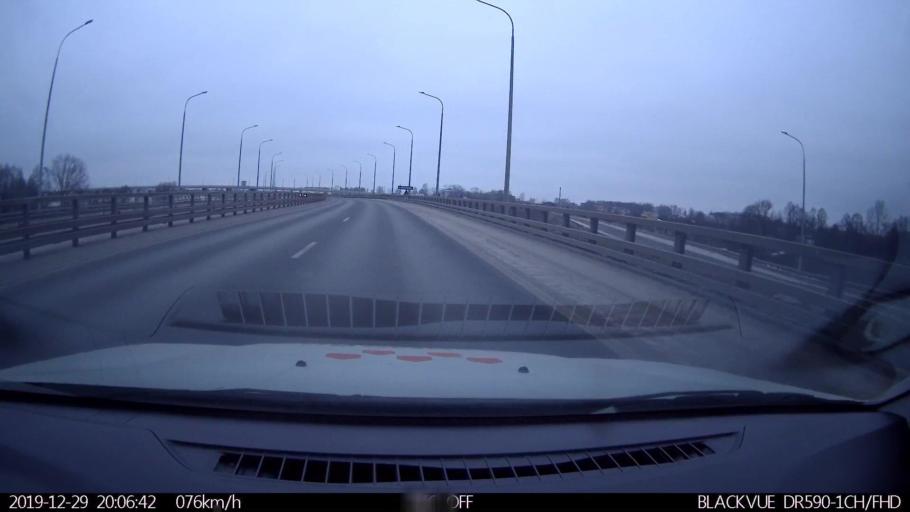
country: RU
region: Nizjnij Novgorod
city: Neklyudovo
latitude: 56.3968
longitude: 43.9975
